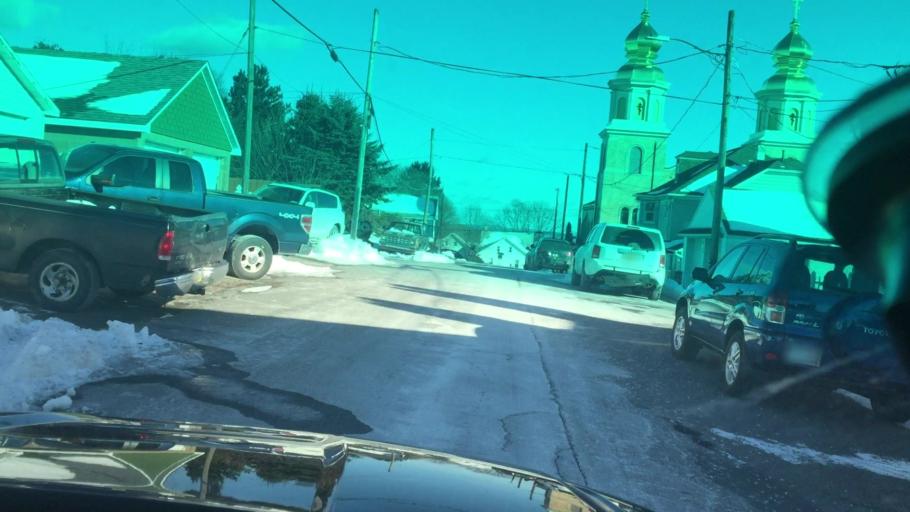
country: US
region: Pennsylvania
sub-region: Luzerne County
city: Freeland
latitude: 41.0187
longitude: -75.9009
